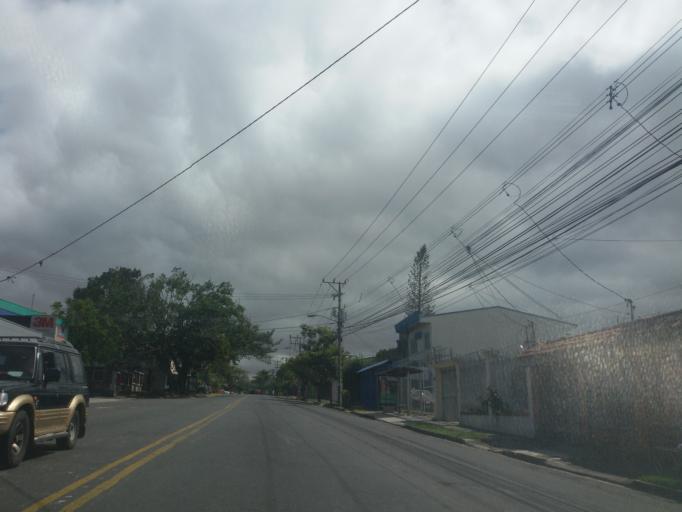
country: CR
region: San Jose
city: Colima
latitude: 9.9568
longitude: -84.1180
